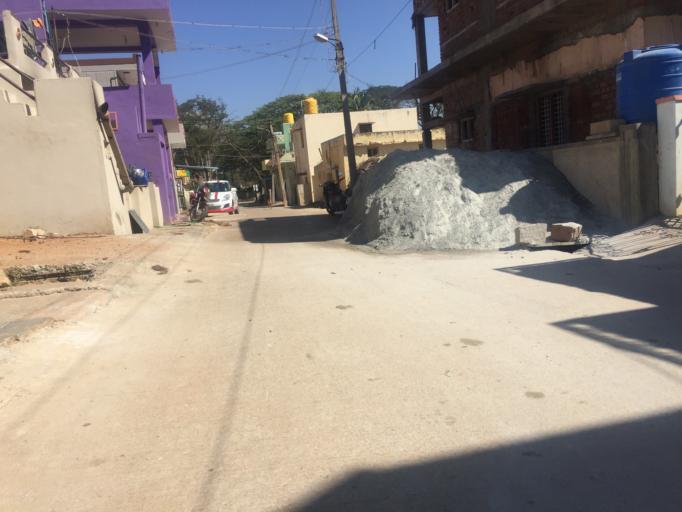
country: IN
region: Karnataka
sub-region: Chikkaballapur
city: Chik Ballapur
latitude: 13.3829
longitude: 77.6832
